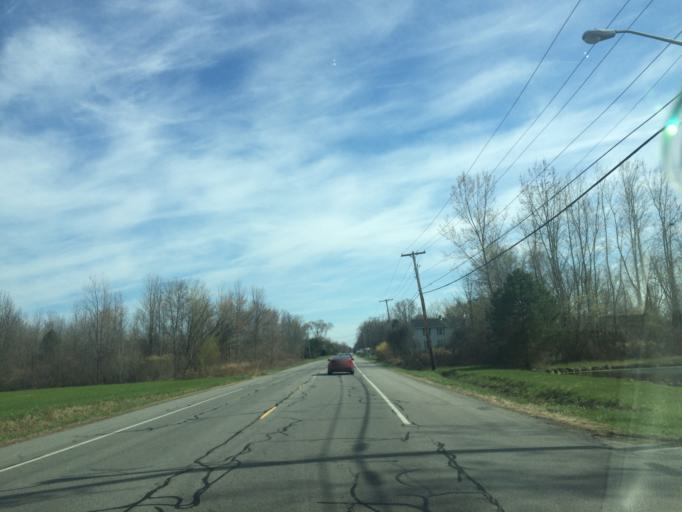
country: US
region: New York
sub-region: Monroe County
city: Webster
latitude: 43.1955
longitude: -77.4304
